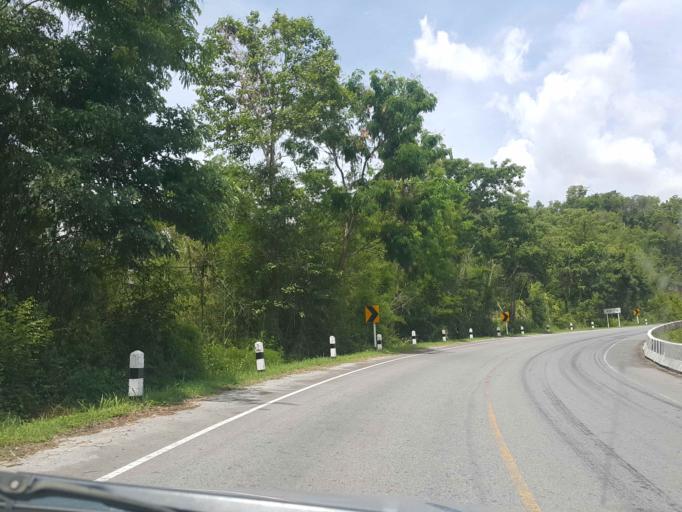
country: TH
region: Nan
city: Ban Luang
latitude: 18.8741
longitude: 100.4923
